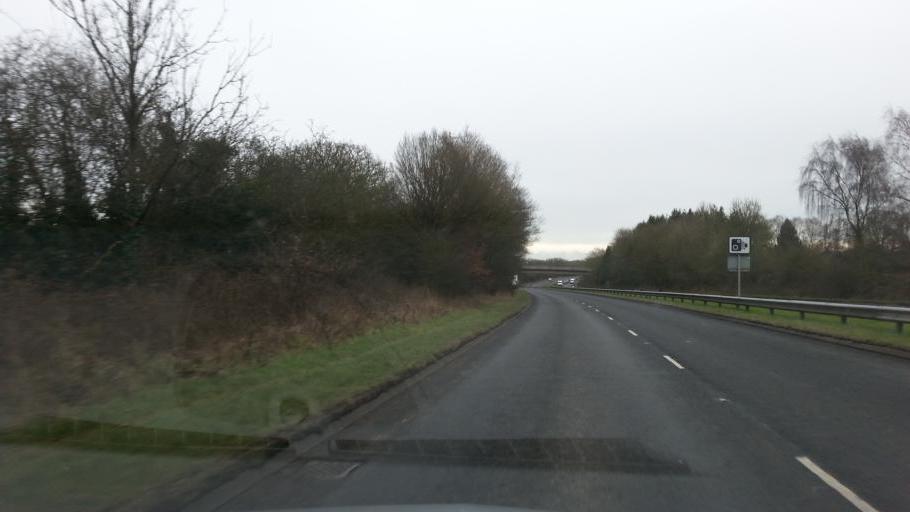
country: GB
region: England
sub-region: Solihull
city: Tidbury Green
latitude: 52.3817
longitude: -1.8933
